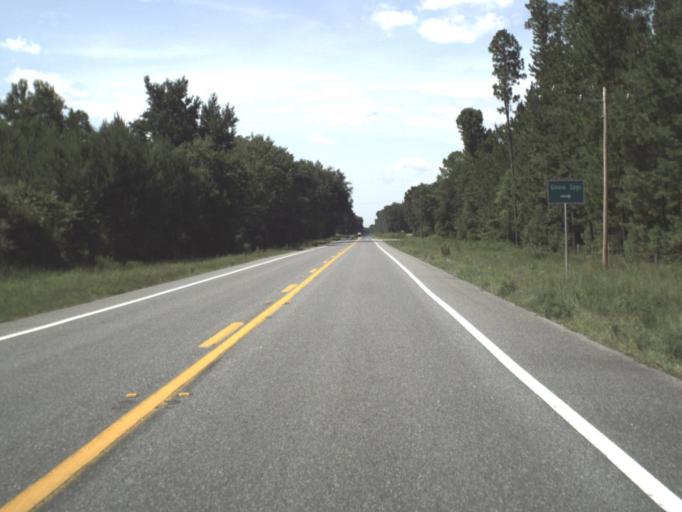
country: US
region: Florida
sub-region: Alachua County
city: High Springs
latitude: 29.8319
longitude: -82.7416
